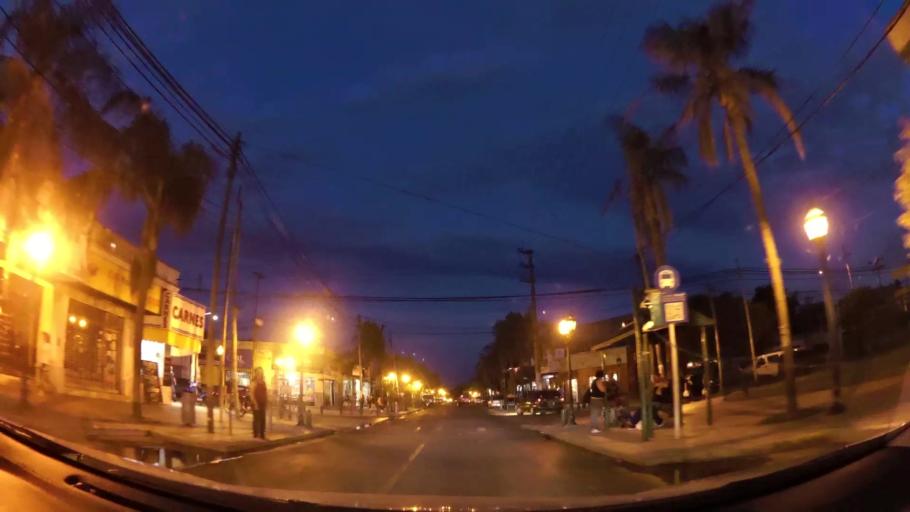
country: AR
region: Buenos Aires
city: Santa Catalina - Dique Lujan
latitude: -34.4113
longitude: -58.6882
